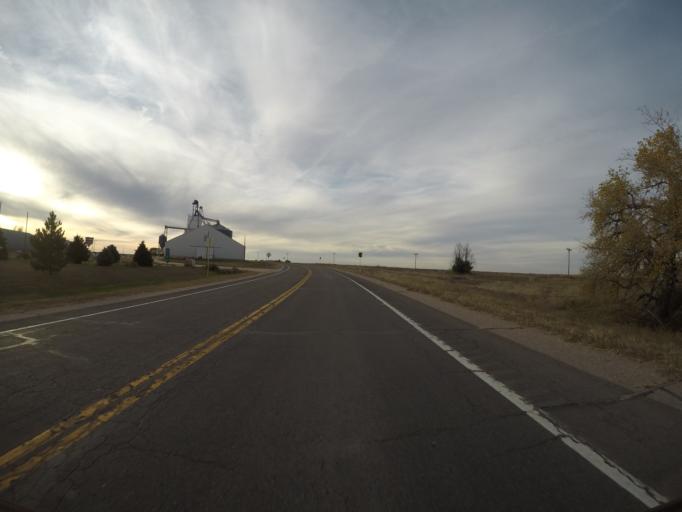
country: US
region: Colorado
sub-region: Yuma County
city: Yuma
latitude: 39.6692
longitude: -102.8527
